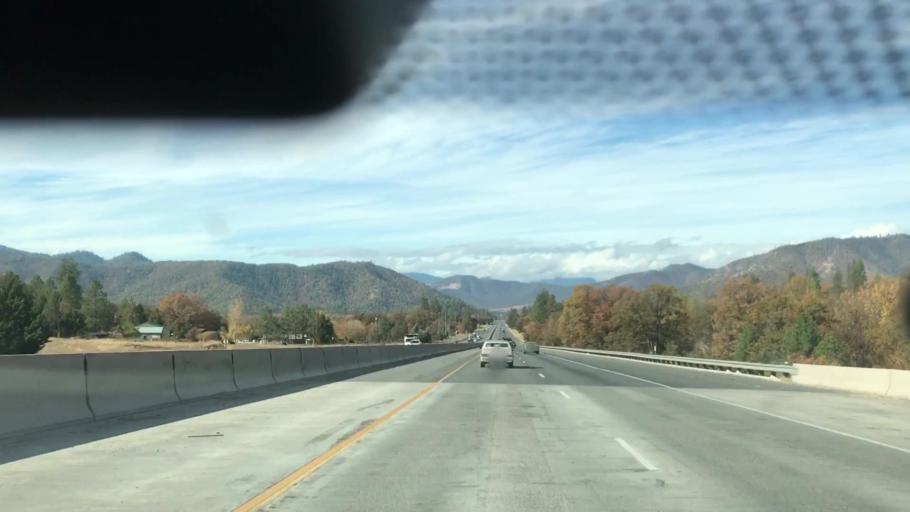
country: US
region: Oregon
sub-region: Jackson County
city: Gold Hill
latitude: 42.4161
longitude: -123.0036
